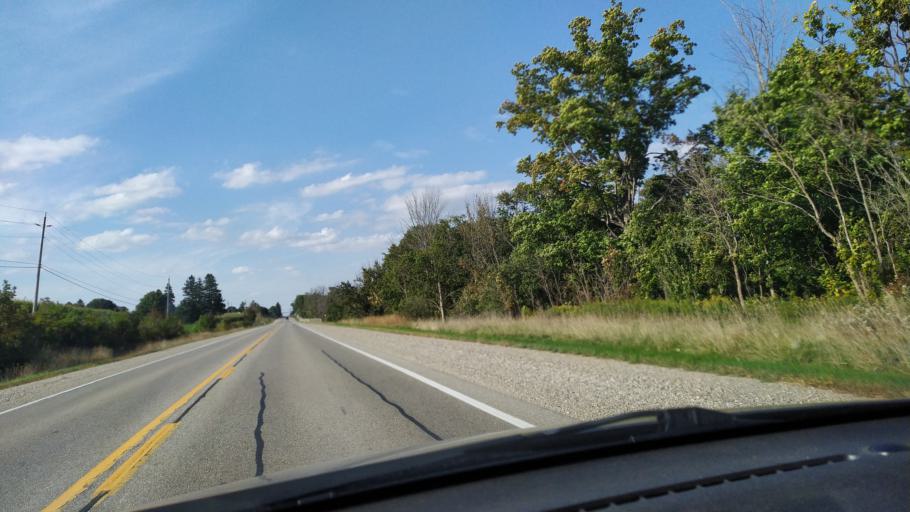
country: CA
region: Ontario
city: Ingersoll
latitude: 43.1440
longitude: -80.8953
